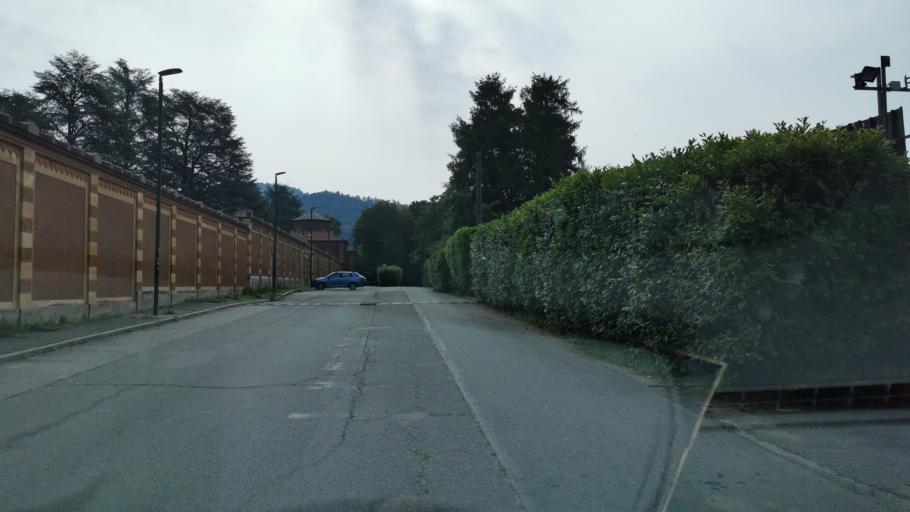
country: IT
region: Piedmont
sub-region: Provincia di Torino
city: Turin
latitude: 45.0817
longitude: 7.7257
